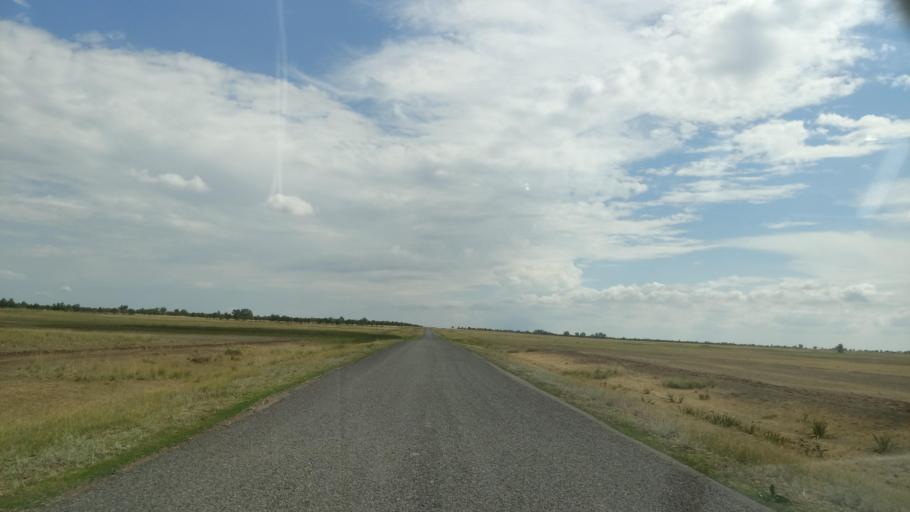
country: KZ
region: Pavlodar
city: Pavlodar
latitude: 52.6364
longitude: 76.9507
